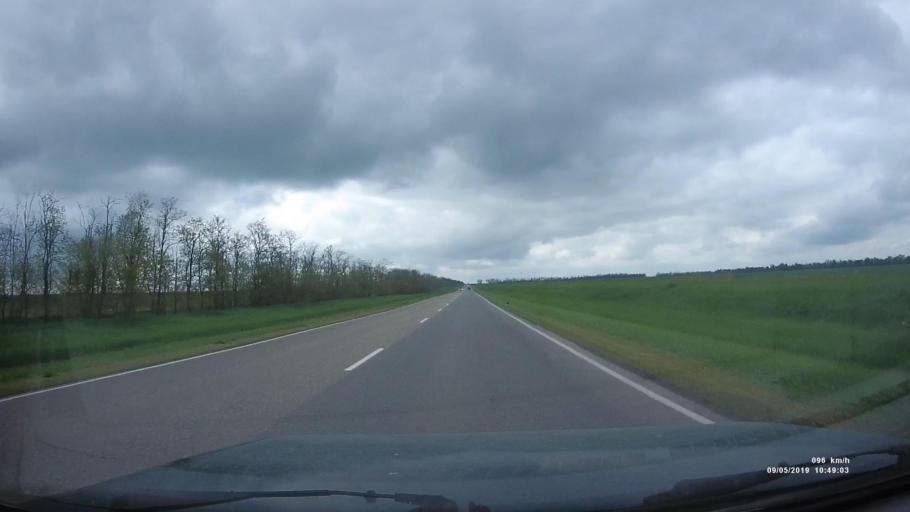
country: RU
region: Rostov
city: Peshkovo
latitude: 46.9484
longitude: 39.3558
